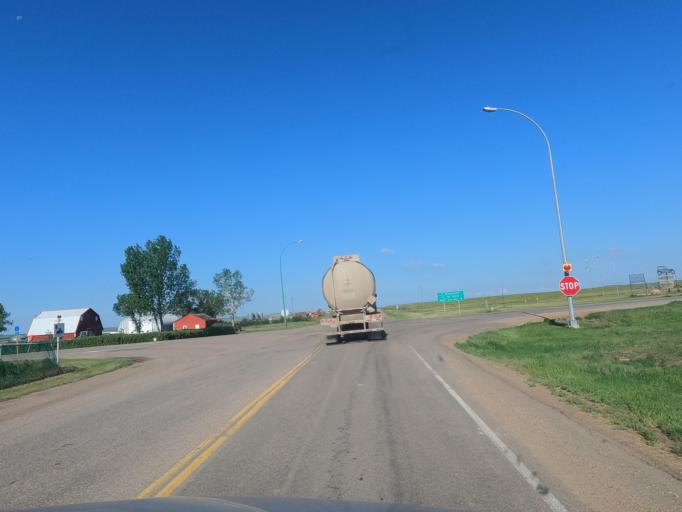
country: CA
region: Saskatchewan
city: Swift Current
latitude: 49.7278
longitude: -107.7432
